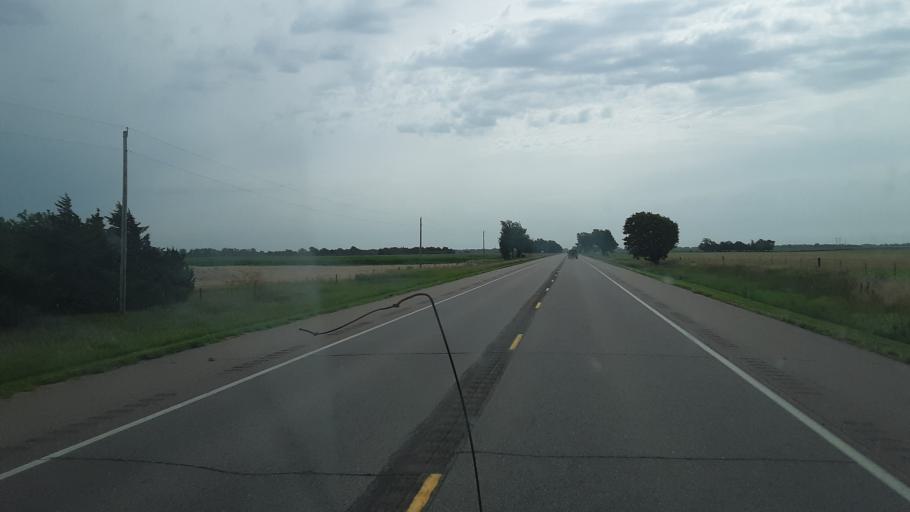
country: US
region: Kansas
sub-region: Stafford County
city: Saint John
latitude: 37.9559
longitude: -98.7651
